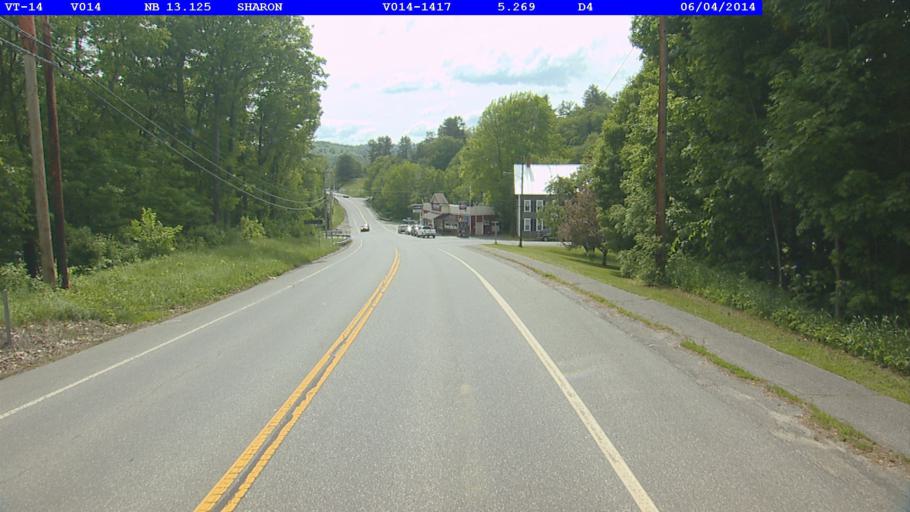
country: US
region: Vermont
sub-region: Windsor County
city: Woodstock
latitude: 43.7833
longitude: -72.4589
